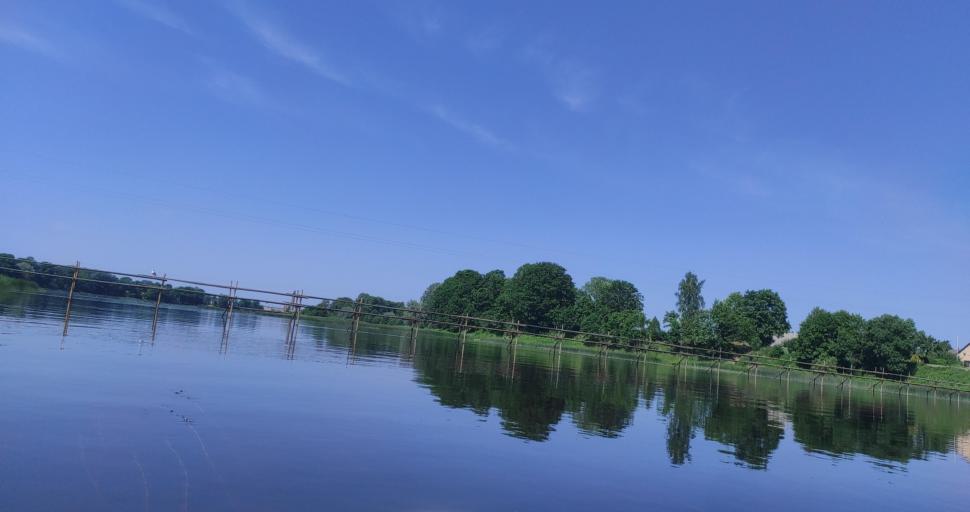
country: LV
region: Salacgrivas
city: Salacgriva
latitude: 57.7524
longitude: 24.3756
